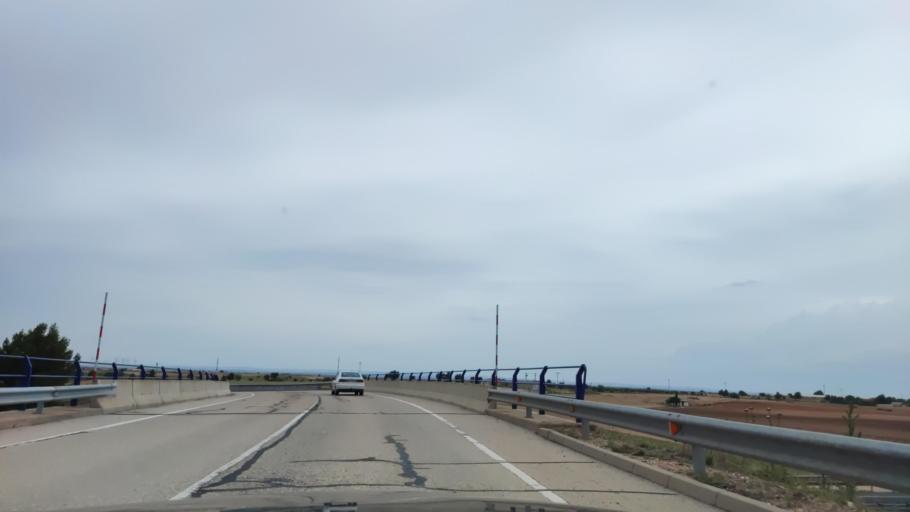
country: ES
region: Castille-La Mancha
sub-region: Provincia de Albacete
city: La Roda
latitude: 39.2209
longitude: -2.1916
